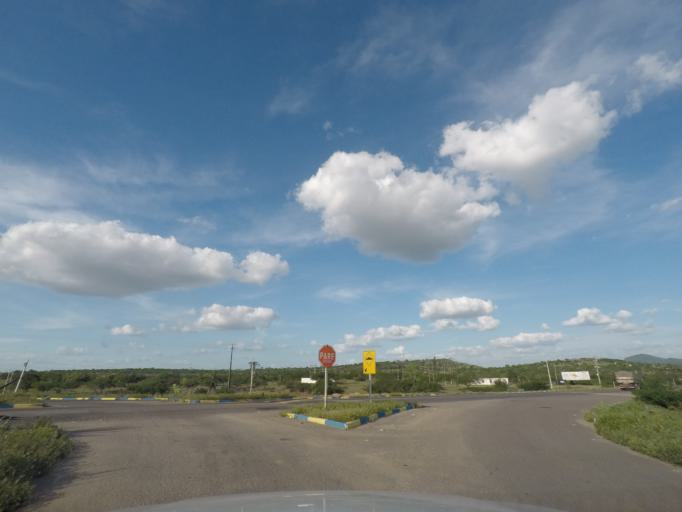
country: BR
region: Bahia
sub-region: Anguera
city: Anguera
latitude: -12.1809
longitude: -39.4530
